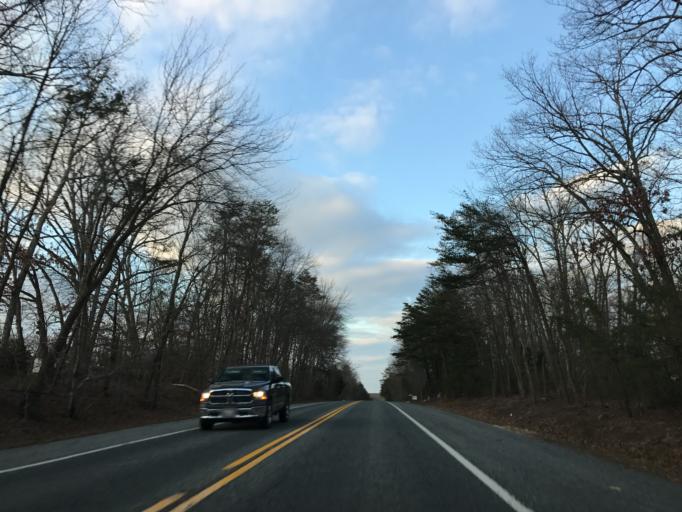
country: US
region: Maryland
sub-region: Cecil County
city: Charlestown
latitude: 39.5252
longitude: -75.9538
